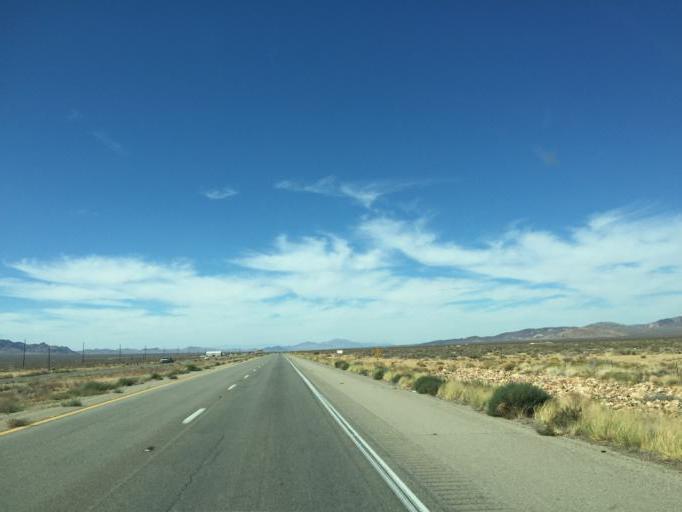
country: US
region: Arizona
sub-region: Mohave County
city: Dolan Springs
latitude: 35.5465
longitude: -114.3639
